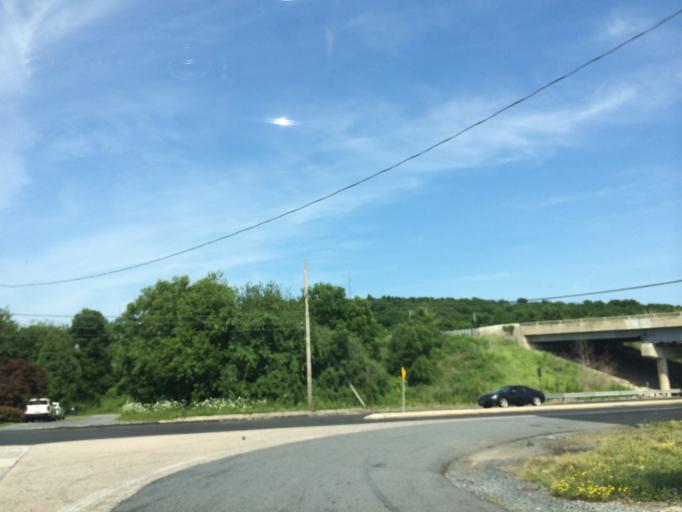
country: US
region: Pennsylvania
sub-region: Berks County
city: Kutztown
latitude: 40.5259
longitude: -75.7814
